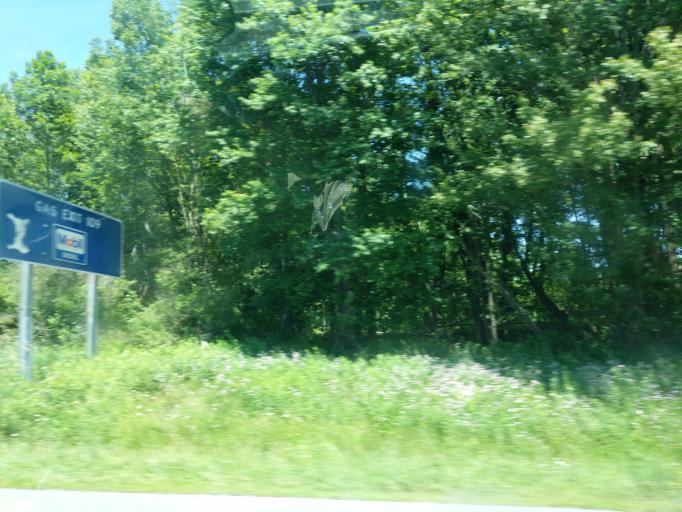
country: US
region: New York
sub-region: Sullivan County
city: Rock Hill
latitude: 41.6232
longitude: -74.5932
